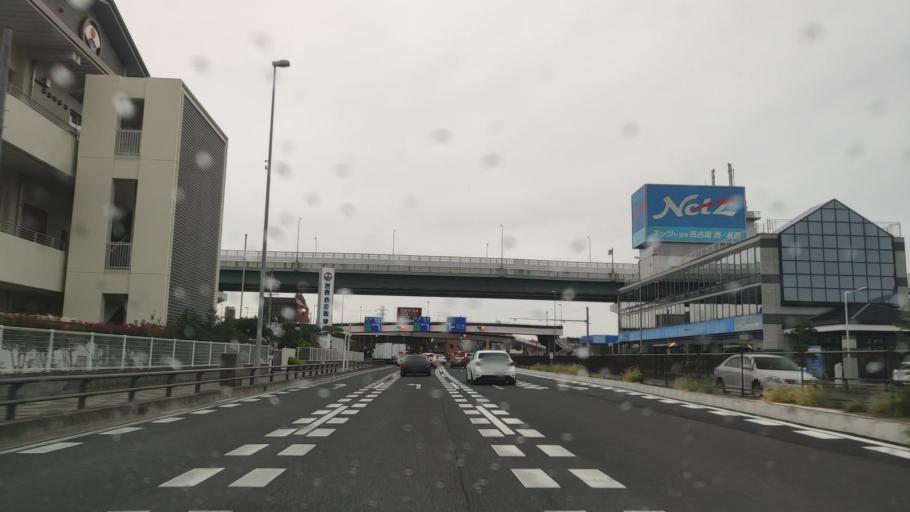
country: JP
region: Aichi
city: Nagoya-shi
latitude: 35.2019
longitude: 136.8814
